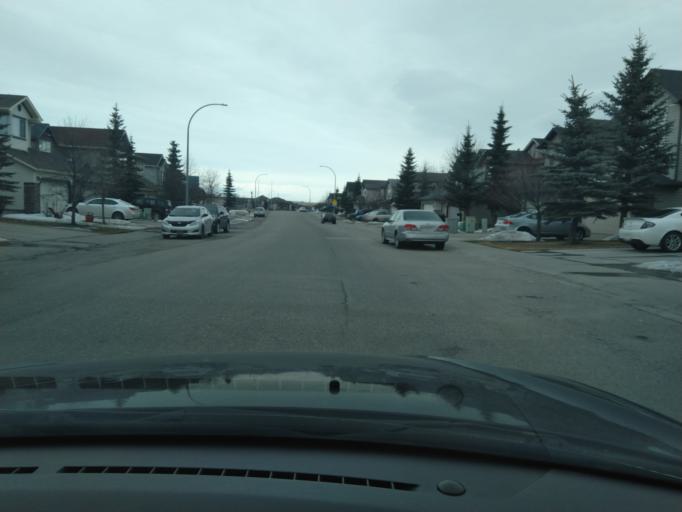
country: CA
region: Alberta
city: Calgary
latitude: 51.1610
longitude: -114.0870
